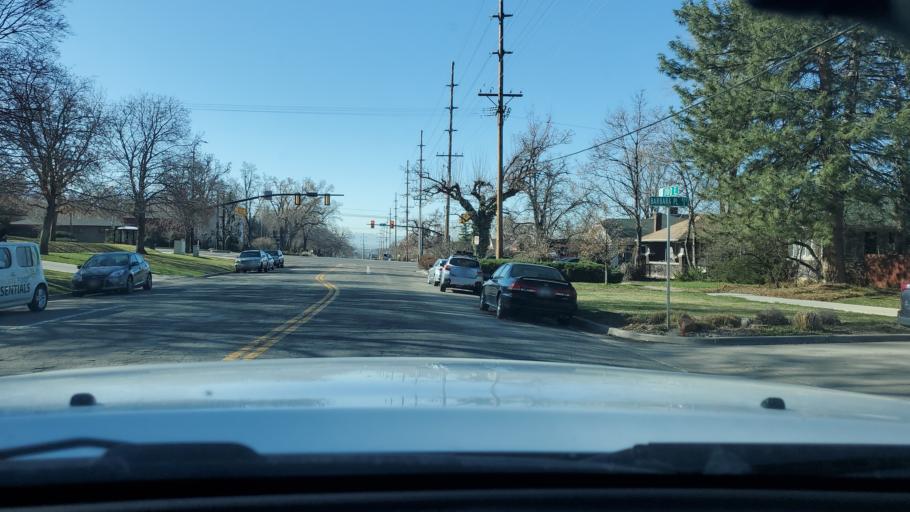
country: US
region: Utah
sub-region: Salt Lake County
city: Salt Lake City
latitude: 40.7594
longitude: -111.8596
